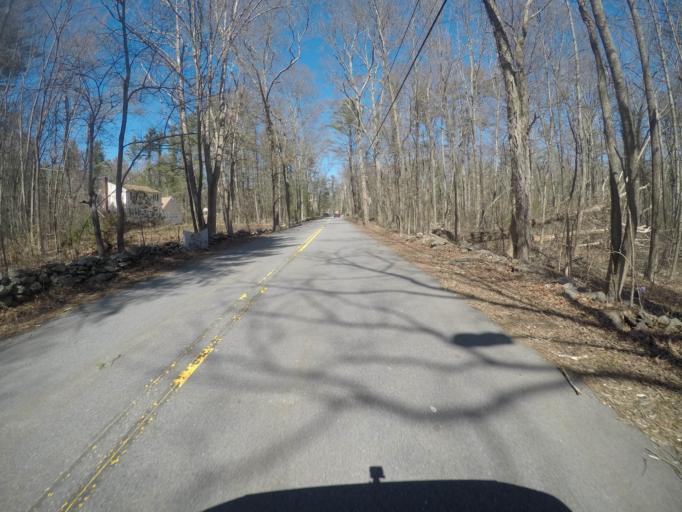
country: US
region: Massachusetts
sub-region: Bristol County
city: Easton
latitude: 41.9937
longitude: -71.1020
